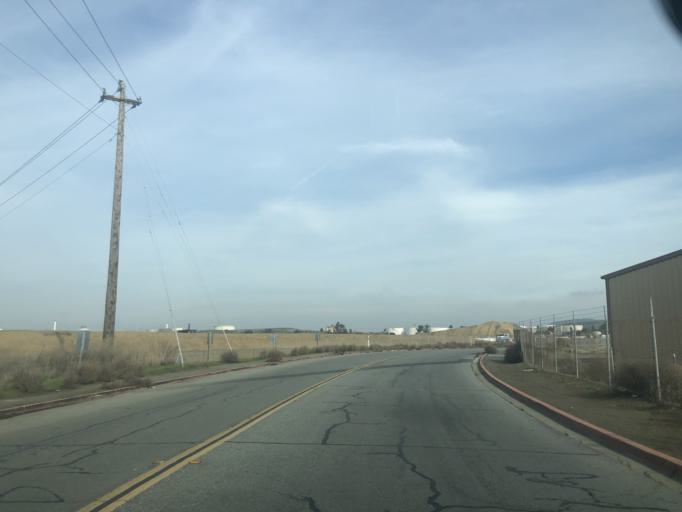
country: US
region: California
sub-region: Contra Costa County
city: Pacheco
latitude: 37.9960
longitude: -122.0632
